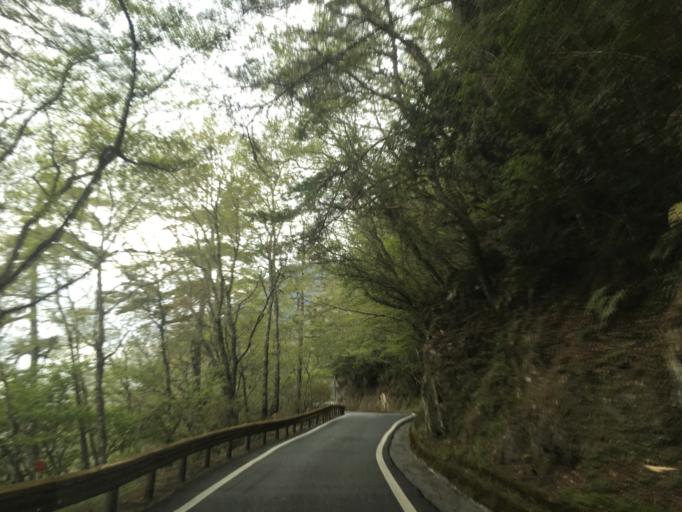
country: TW
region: Taiwan
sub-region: Hualien
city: Hualian
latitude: 24.1728
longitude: 121.3792
